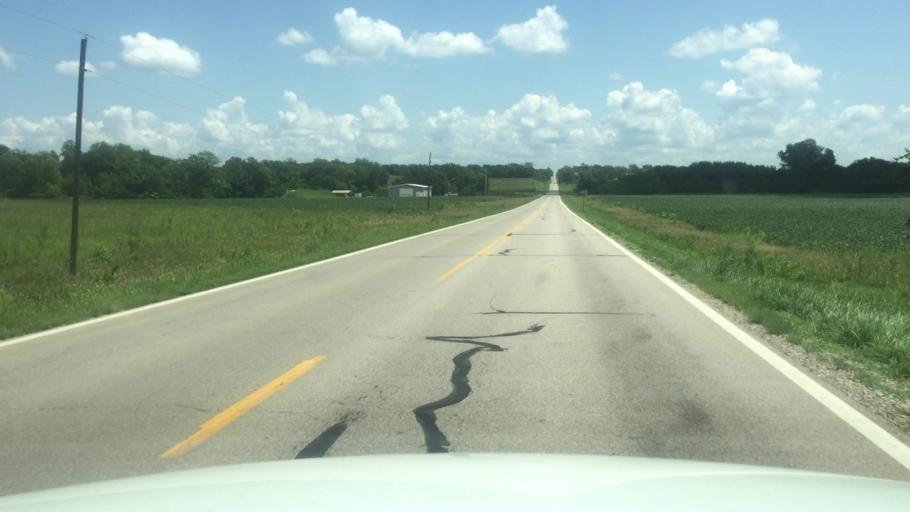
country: US
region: Kansas
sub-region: Brown County
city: Horton
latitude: 39.6673
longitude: -95.5534
